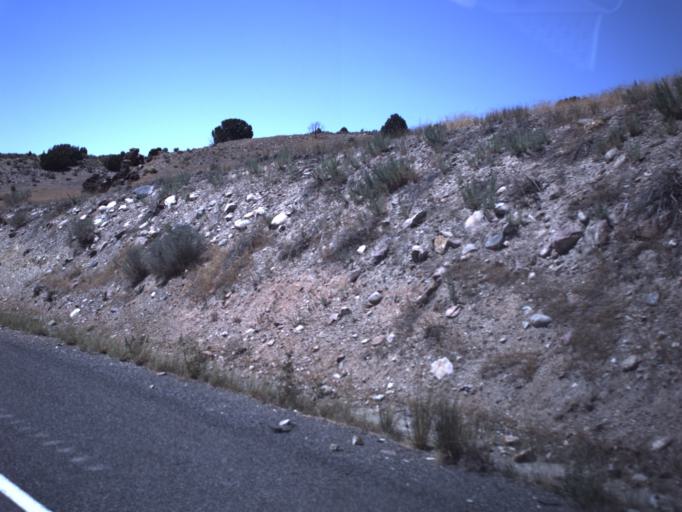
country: US
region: Utah
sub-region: Juab County
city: Nephi
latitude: 39.5989
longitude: -112.1453
